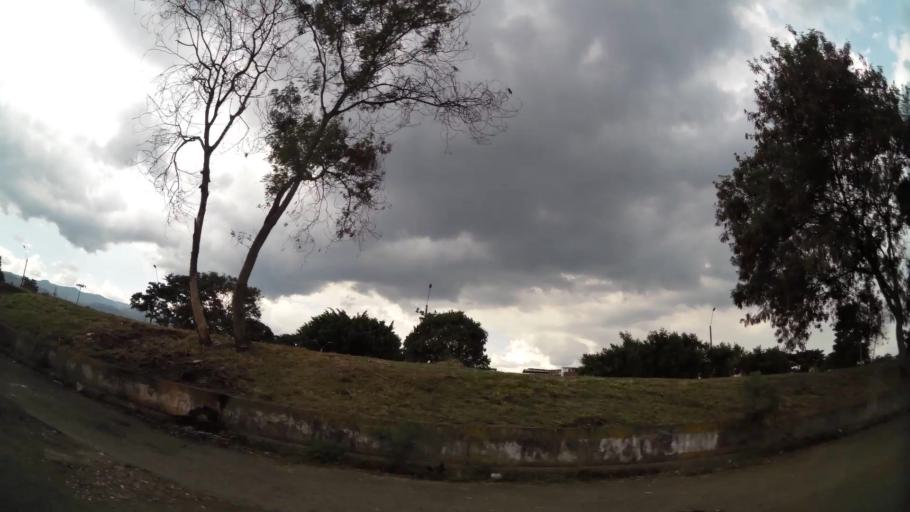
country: CO
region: Valle del Cauca
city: Cali
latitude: 3.4644
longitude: -76.4875
